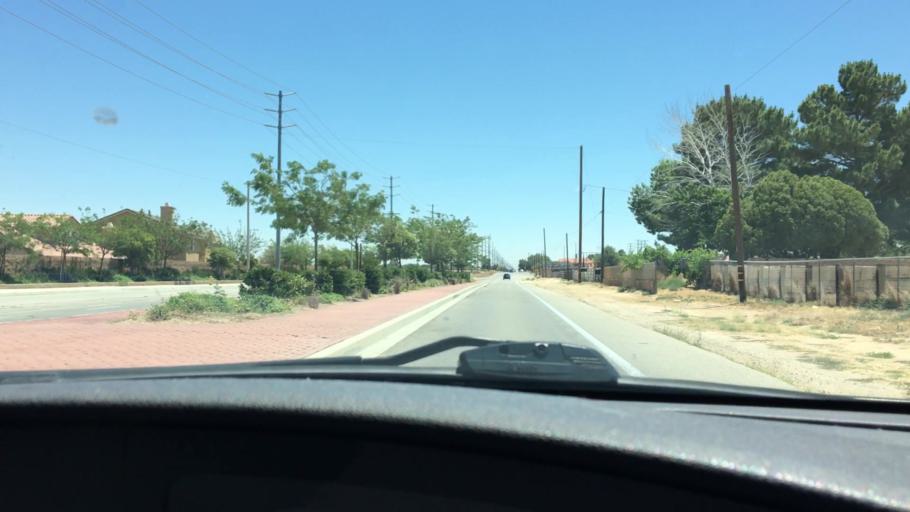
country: US
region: California
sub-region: Los Angeles County
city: Quartz Hill
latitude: 34.6601
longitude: -118.2347
